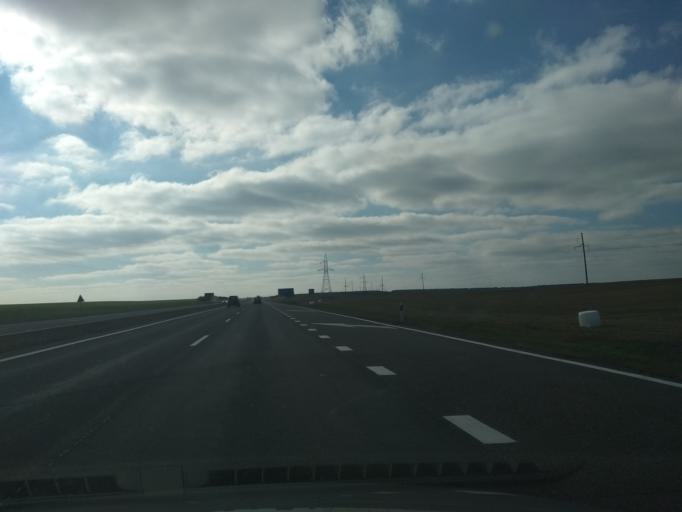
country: BY
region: Grodnenskaya
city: Mir
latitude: 53.4437
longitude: 26.5932
